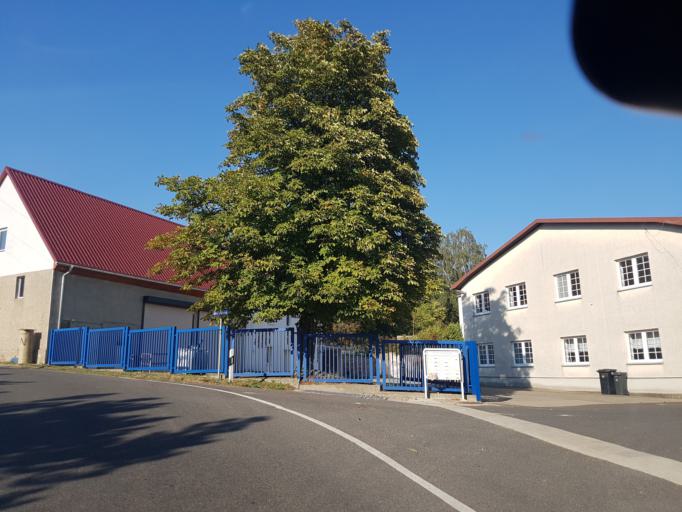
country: DE
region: Saxony
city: Ostrau
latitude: 51.1865
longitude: 13.1107
